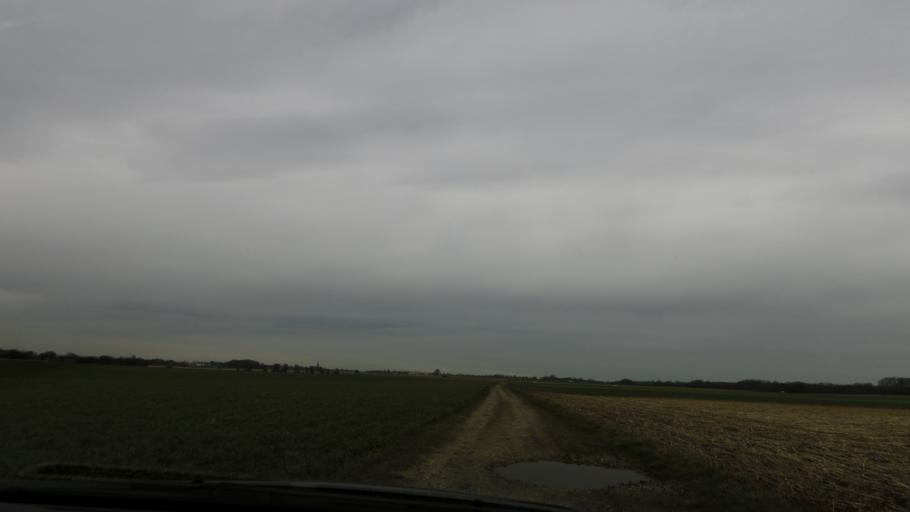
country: DE
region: North Rhine-Westphalia
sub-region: Regierungsbezirk Koln
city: Ubach-Palenberg
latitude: 50.9376
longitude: 6.0539
